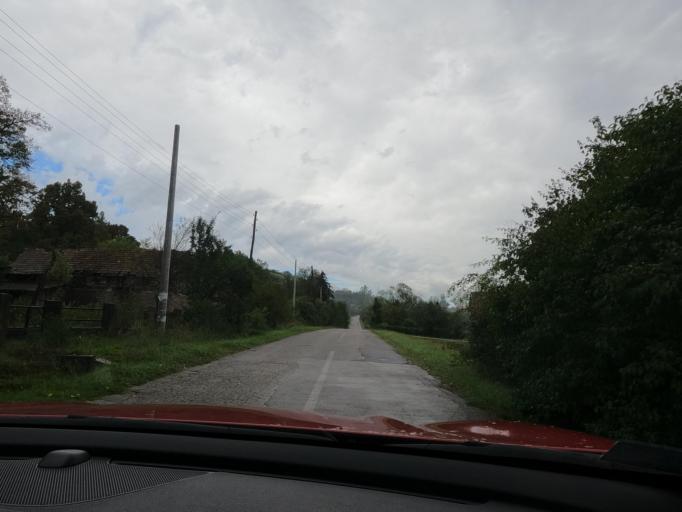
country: HR
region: Sisacko-Moslavacka
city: Glina
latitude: 45.3126
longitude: 16.1925
